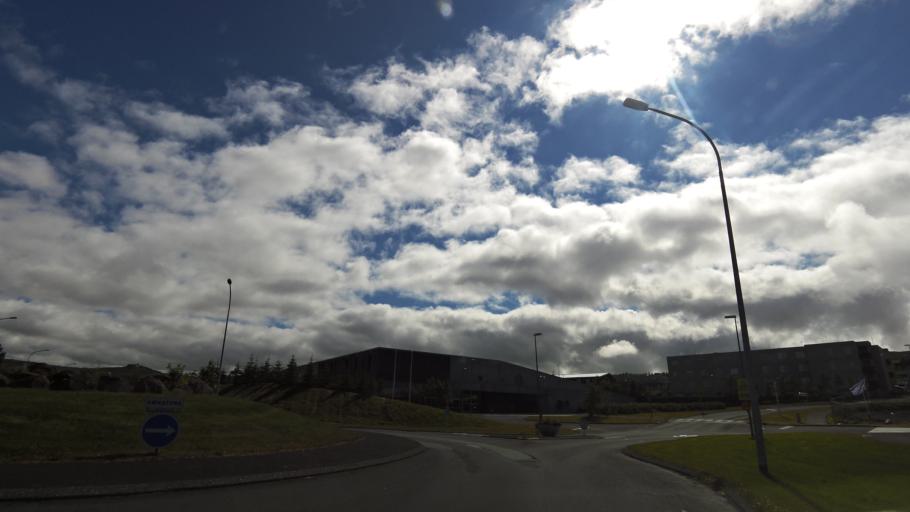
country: IS
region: Capital Region
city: Mosfellsbaer
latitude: 64.1638
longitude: -21.6889
